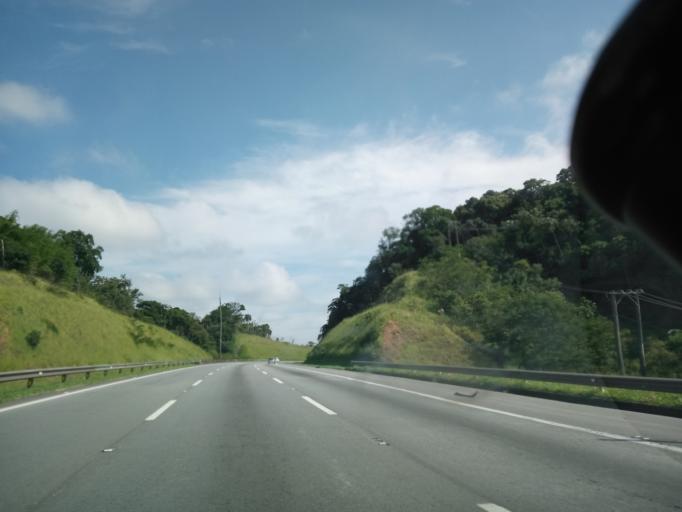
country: BR
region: Sao Paulo
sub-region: Embu
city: Embu
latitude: -23.6748
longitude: -46.8236
